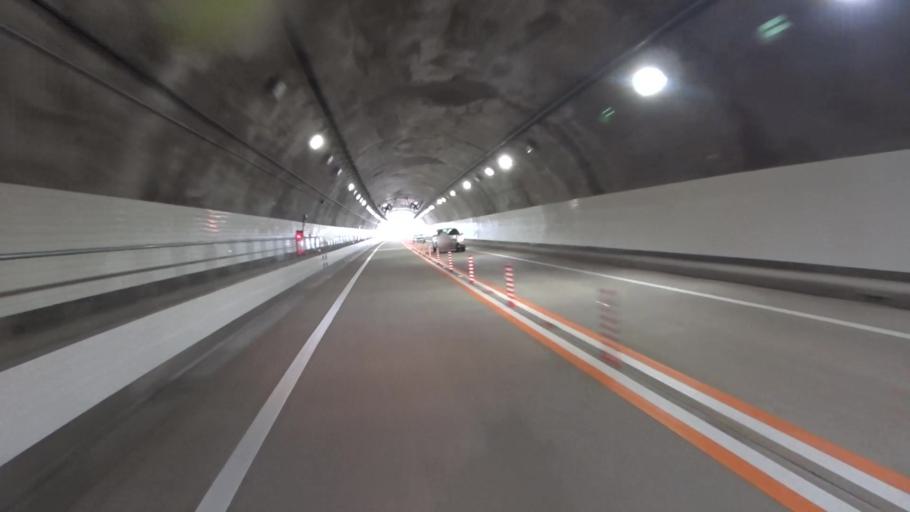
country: JP
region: Kyoto
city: Ayabe
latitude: 35.2303
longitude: 135.3446
